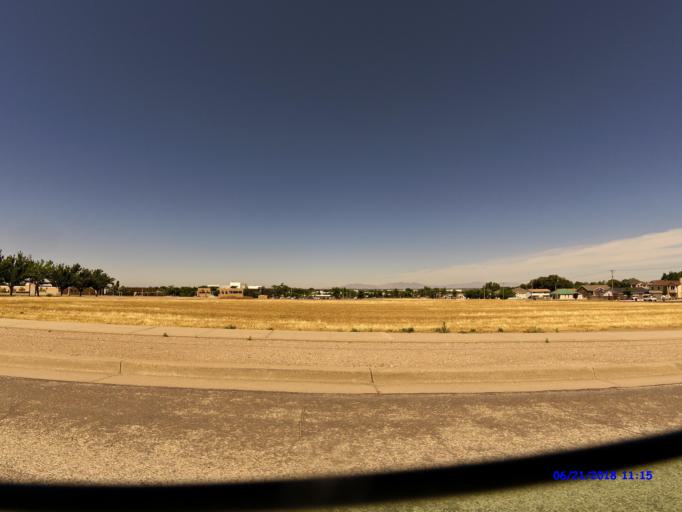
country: US
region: Utah
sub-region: Weber County
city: Harrisville
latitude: 41.2658
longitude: -111.9593
